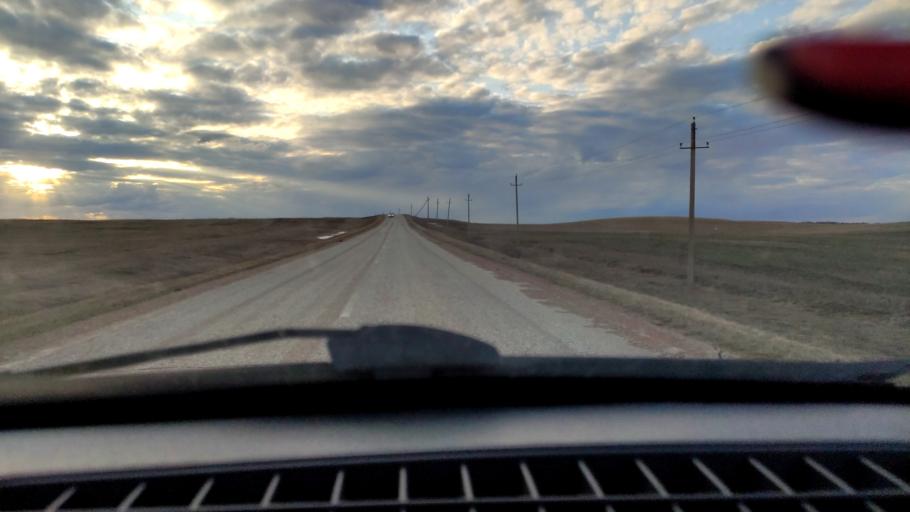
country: RU
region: Bashkortostan
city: Tolbazy
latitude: 54.0017
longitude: 55.6548
